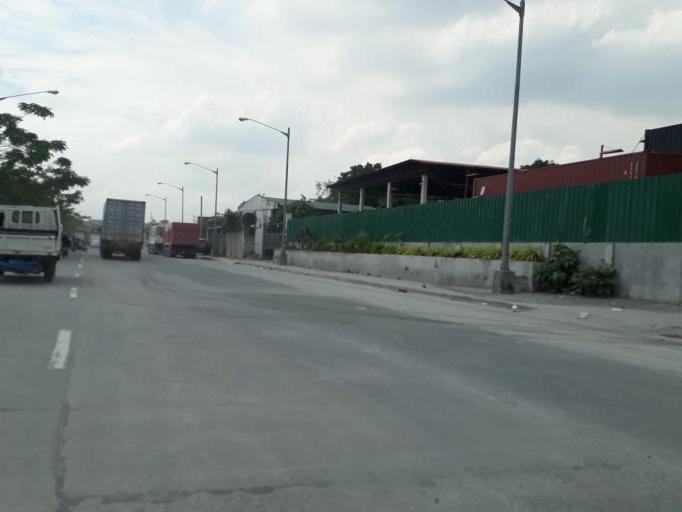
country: PH
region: Calabarzon
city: Bagong Pagasa
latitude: 14.6953
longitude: 121.0203
